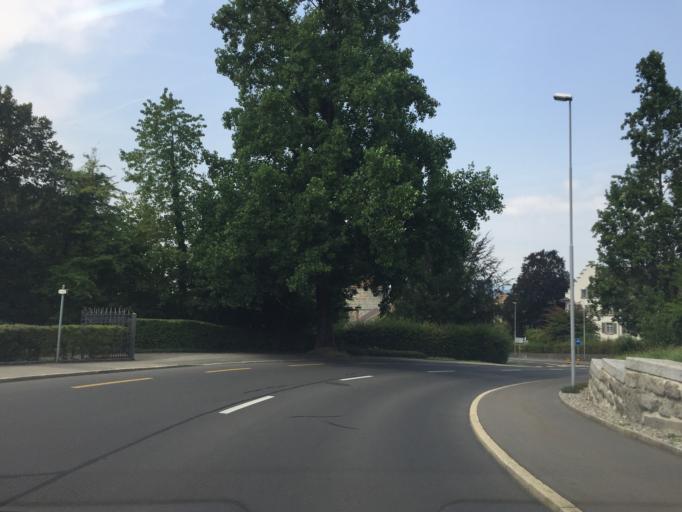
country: CH
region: Zug
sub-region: Zug
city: Zug
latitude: 47.1627
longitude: 8.5172
